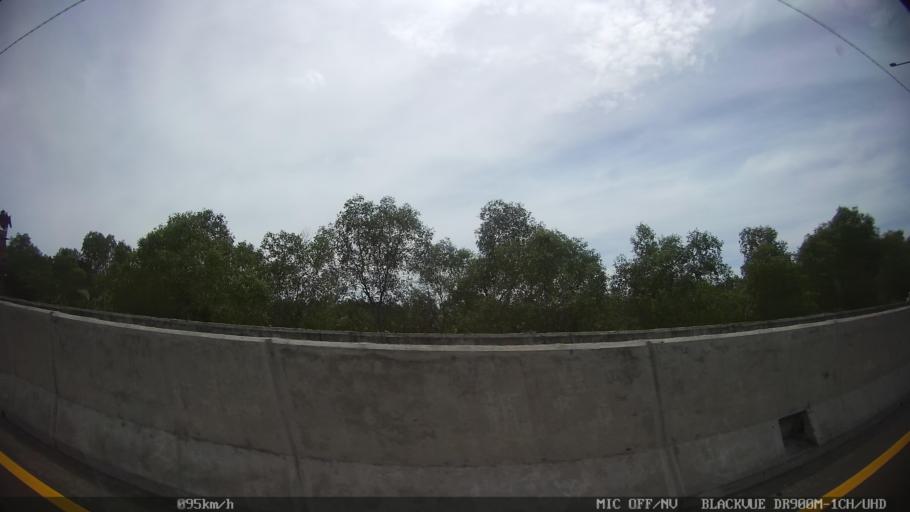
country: ID
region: North Sumatra
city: Belawan
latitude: 3.7539
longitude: 98.6824
